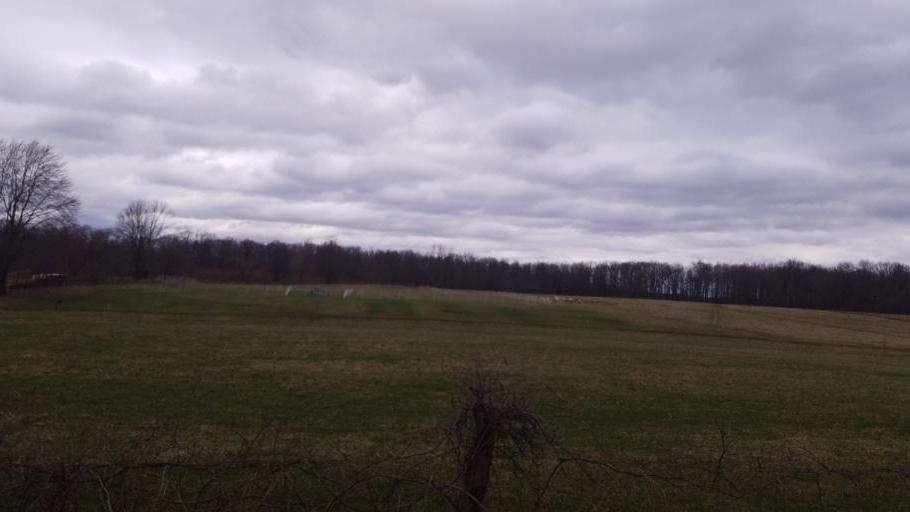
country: US
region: Ohio
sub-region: Knox County
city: Centerburg
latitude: 40.4326
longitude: -82.6645
